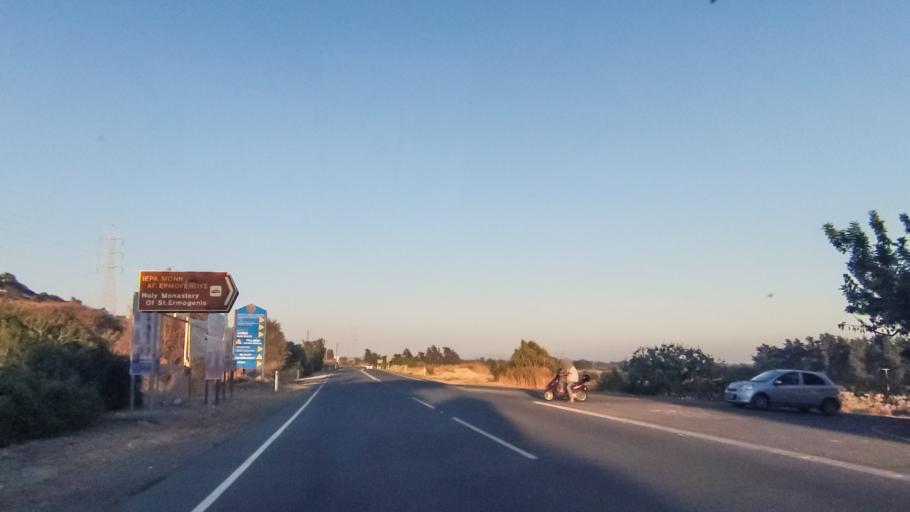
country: CY
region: Limassol
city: Erimi
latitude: 34.6646
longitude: 32.8937
